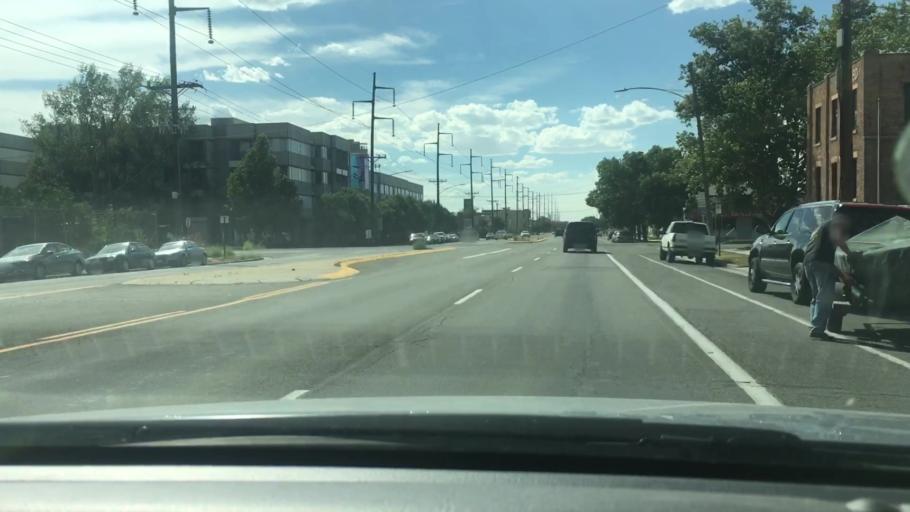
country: US
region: Utah
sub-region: Salt Lake County
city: Salt Lake City
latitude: 40.7520
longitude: -111.9017
